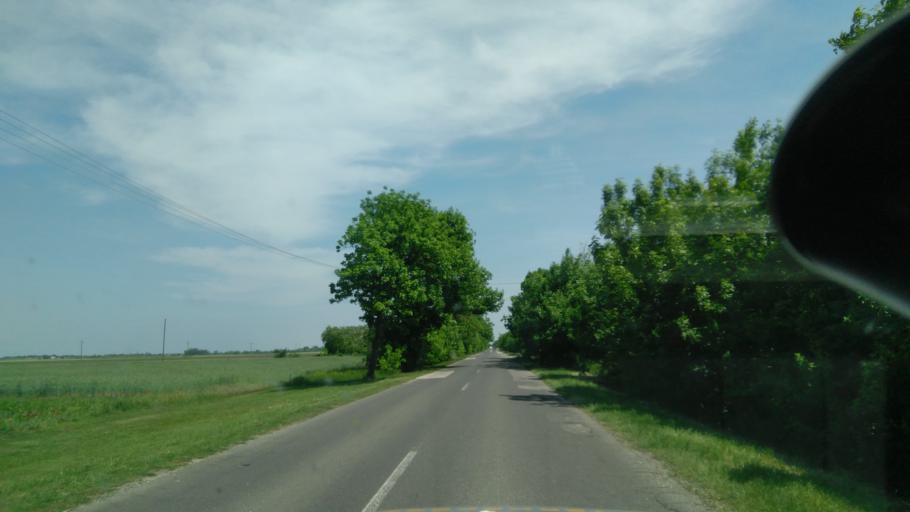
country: HU
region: Csongrad
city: Szekkutas
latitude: 46.5696
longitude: 20.5669
